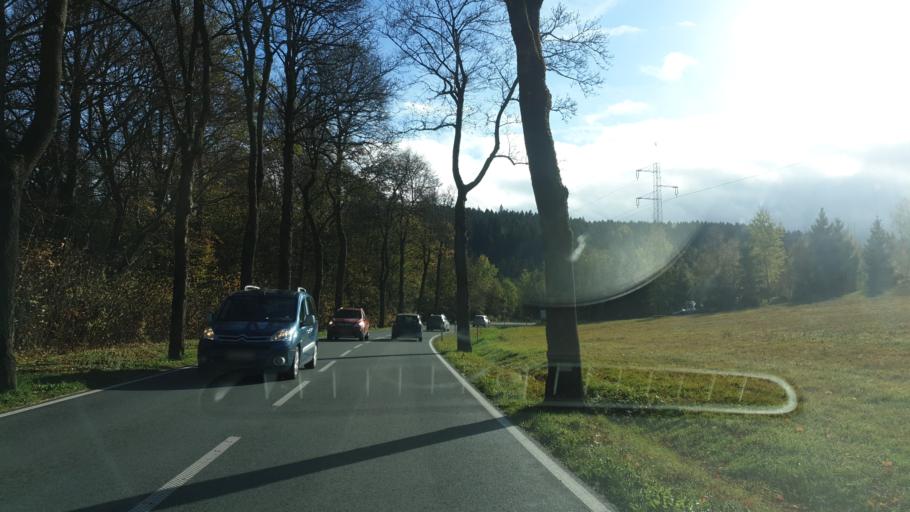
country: DE
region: Saxony
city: Sosa
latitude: 50.5189
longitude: 12.6347
